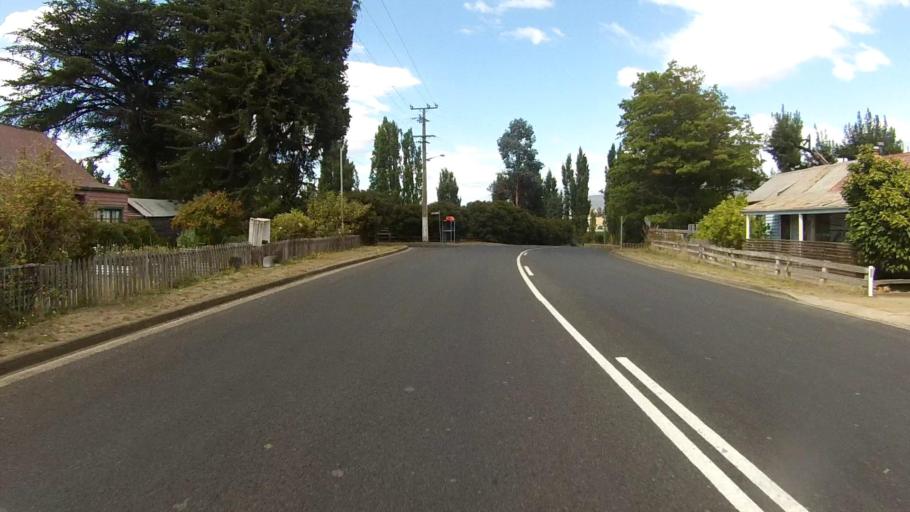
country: AU
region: Tasmania
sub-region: Derwent Valley
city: New Norfolk
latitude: -42.6984
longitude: 146.8905
